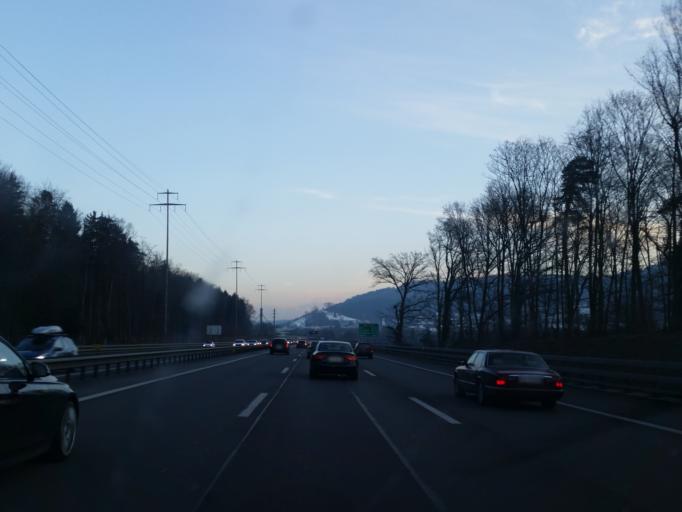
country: CH
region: Aargau
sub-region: Bezirk Baden
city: Killwangen
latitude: 47.4463
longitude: 8.3410
